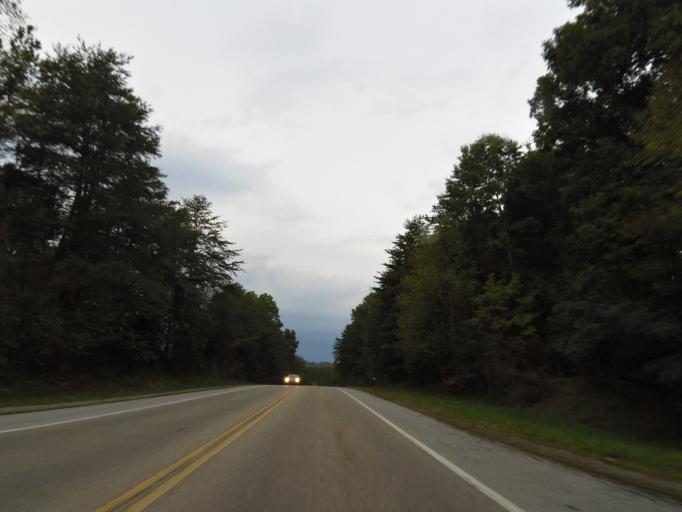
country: US
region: Tennessee
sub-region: Loudon County
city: Loudon
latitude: 35.6856
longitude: -84.2631
